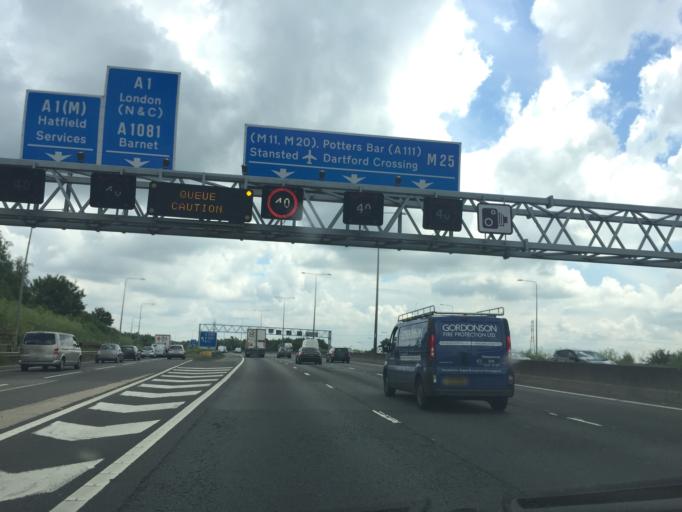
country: GB
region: England
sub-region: Greater London
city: High Barnet
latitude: 51.6897
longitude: -0.2340
